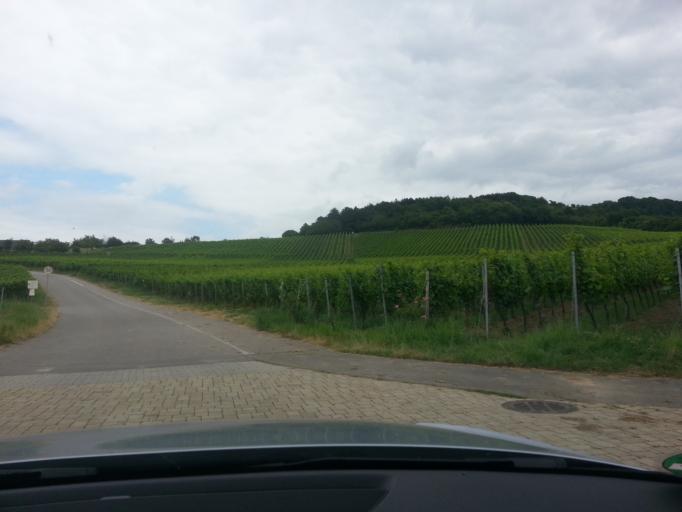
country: DE
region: Saarland
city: Perl
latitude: 49.4645
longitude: 6.3761
